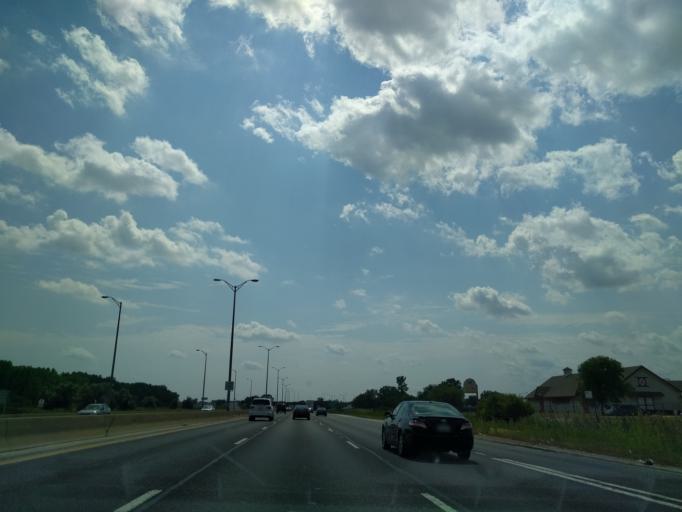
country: US
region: Illinois
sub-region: Cook County
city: Dolton
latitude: 41.6903
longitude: -87.5994
